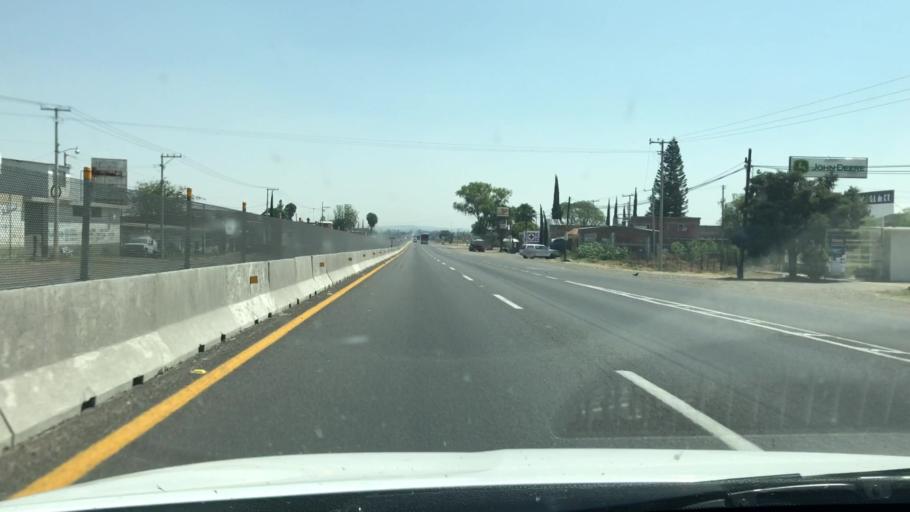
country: MX
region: Guanajuato
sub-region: Abasolo
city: San Bernardo Pena Blanca
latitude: 20.4679
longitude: -101.5065
